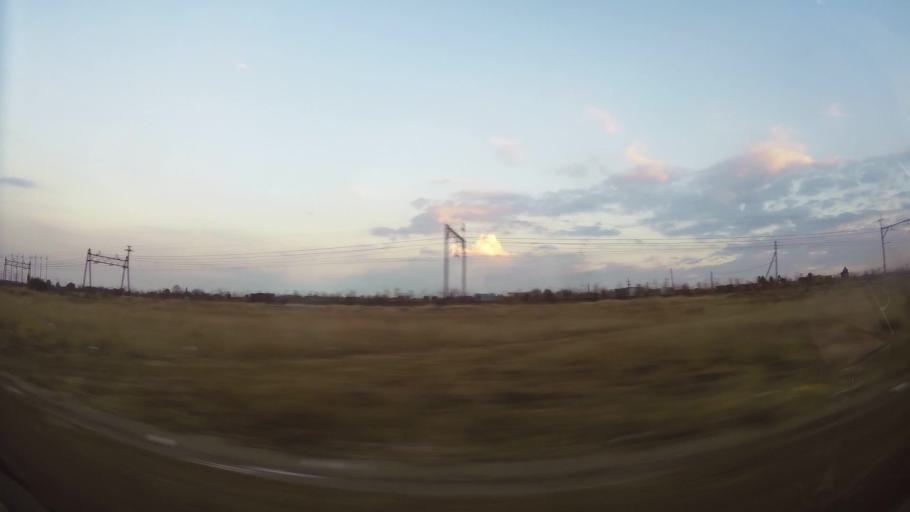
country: ZA
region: Gauteng
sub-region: City of Johannesburg Metropolitan Municipality
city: Orange Farm
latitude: -26.5622
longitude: 27.8720
